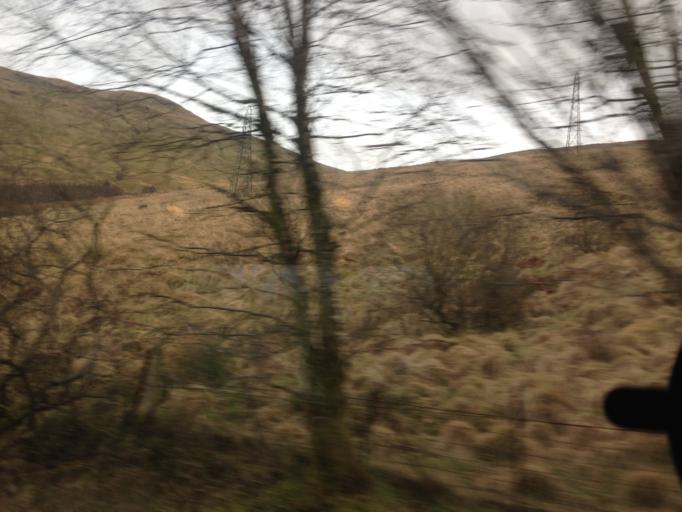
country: GB
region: Scotland
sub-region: Argyll and Bute
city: Garelochhead
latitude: 56.1905
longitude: -4.7534
